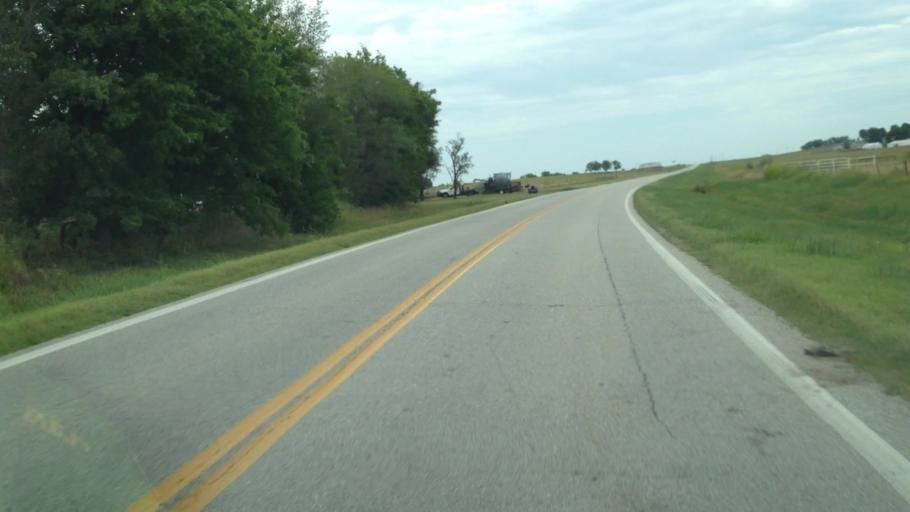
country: US
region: Oklahoma
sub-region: Craig County
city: Vinita
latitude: 36.8222
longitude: -95.1427
